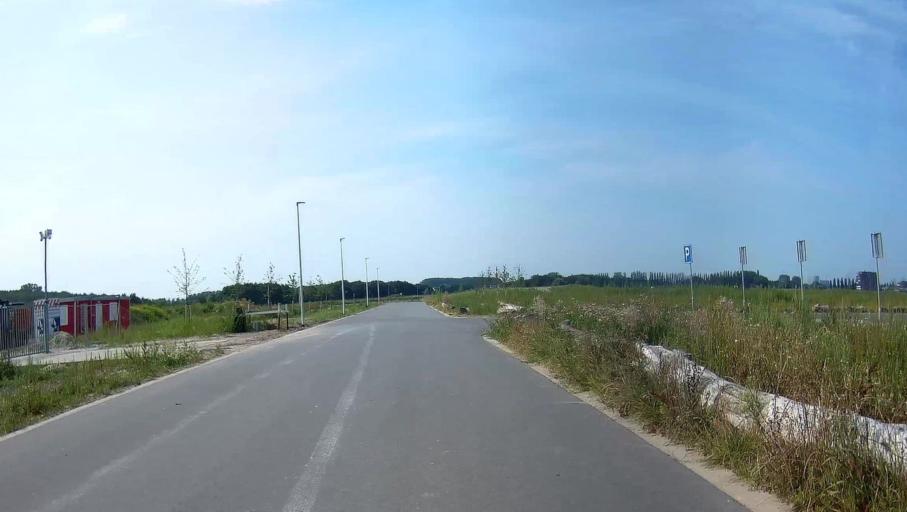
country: NL
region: South Holland
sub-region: Gemeente Pijnacker-Nootdorp
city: Pijnacker
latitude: 52.0595
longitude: 4.4351
